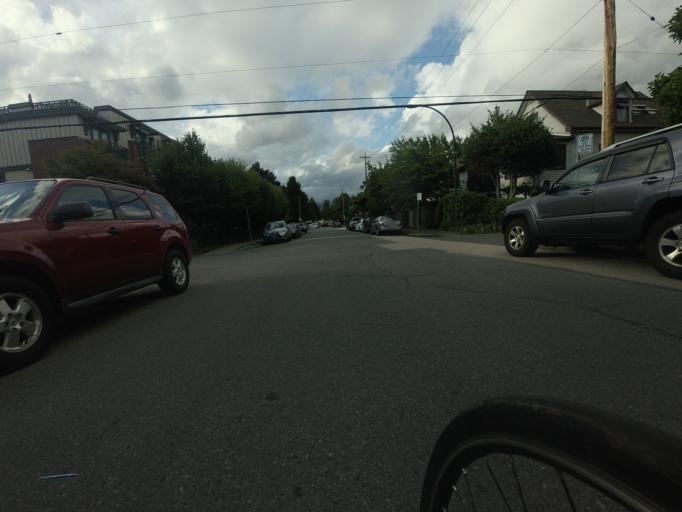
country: CA
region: British Columbia
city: West End
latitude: 49.2702
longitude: -123.1504
